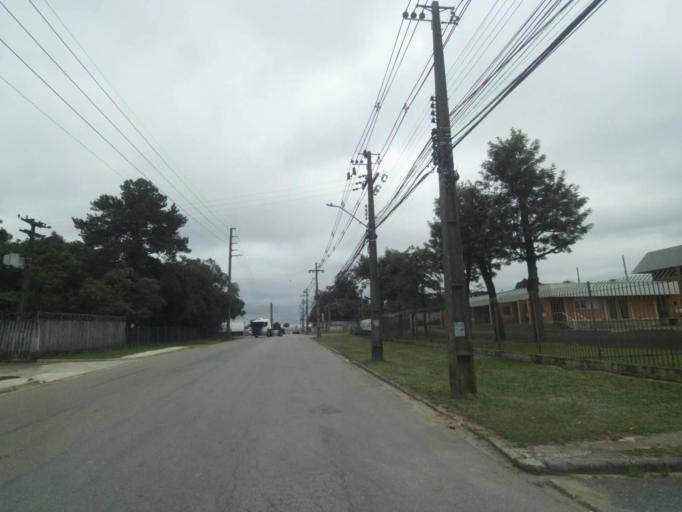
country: BR
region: Parana
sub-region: Sao Jose Dos Pinhais
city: Sao Jose dos Pinhais
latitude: -25.5564
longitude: -49.3090
